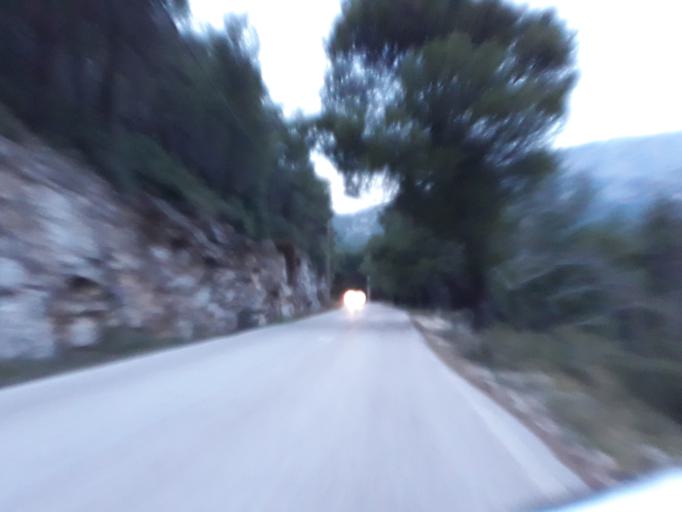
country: GR
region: Attica
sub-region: Nomarchia Dytikis Attikis
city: Fyli
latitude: 38.1213
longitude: 23.6573
